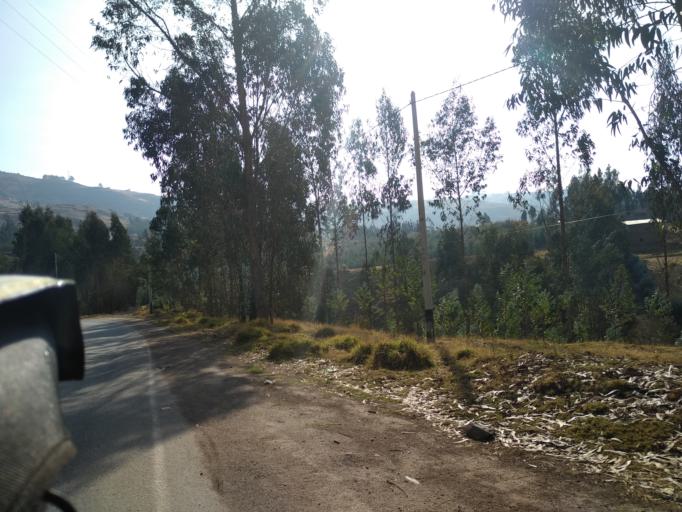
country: PE
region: La Libertad
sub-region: Provincia de Otuzco
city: Agallpampa
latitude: -7.9964
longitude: -78.5191
